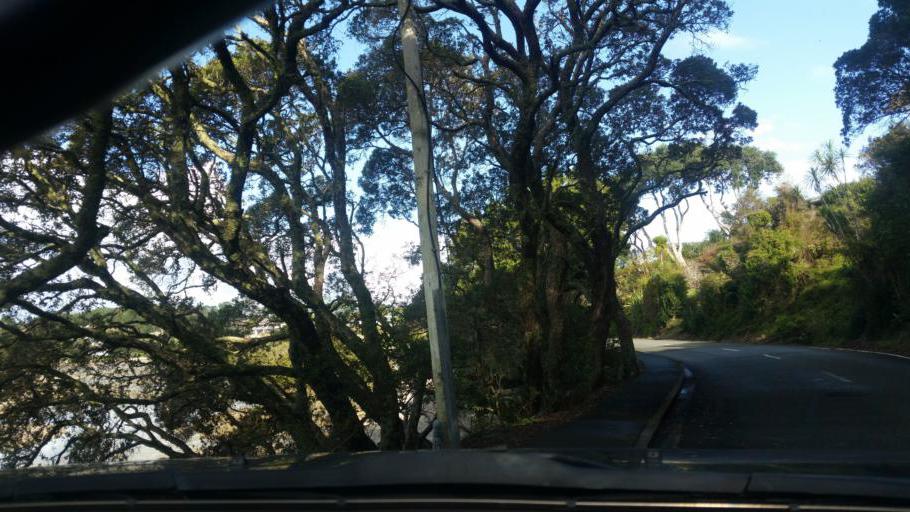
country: NZ
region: Auckland
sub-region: Auckland
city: Wellsford
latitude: -36.2517
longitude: 174.2479
